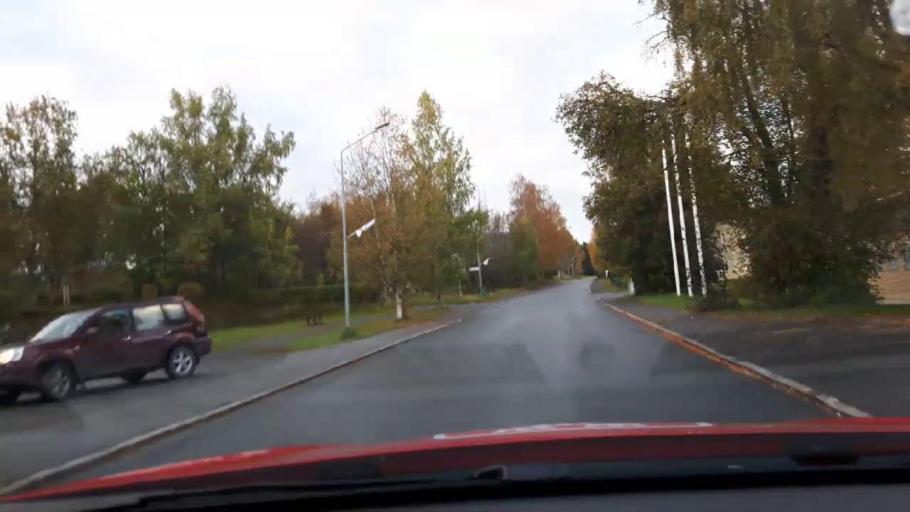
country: SE
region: Jaemtland
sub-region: OEstersunds Kommun
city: Lit
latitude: 63.3172
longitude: 14.8458
